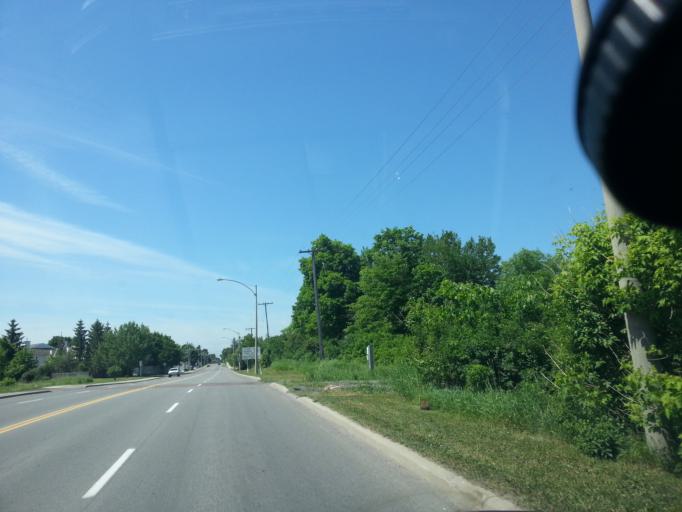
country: CA
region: Ontario
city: Carleton Place
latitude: 45.1489
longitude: -76.1429
